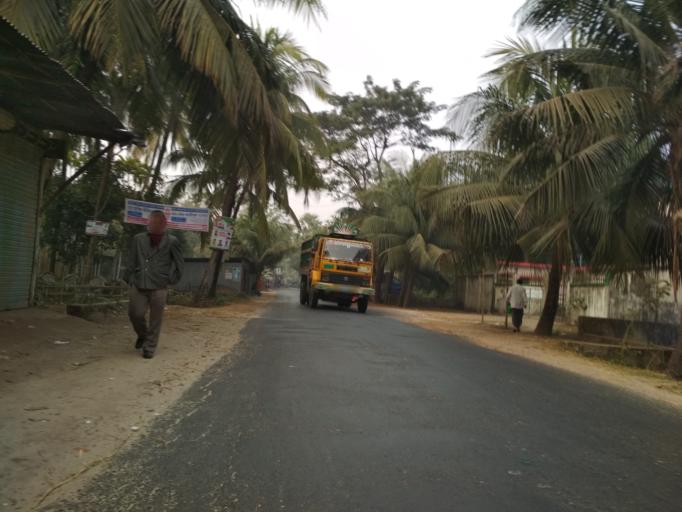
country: BD
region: Chittagong
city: Lakshmipur
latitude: 22.9247
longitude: 90.8342
